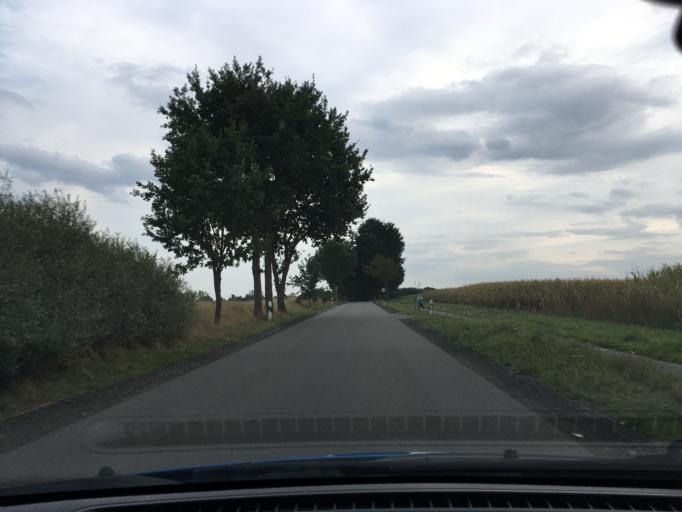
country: DE
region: Lower Saxony
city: Reppenstedt
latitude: 53.2431
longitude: 10.3661
